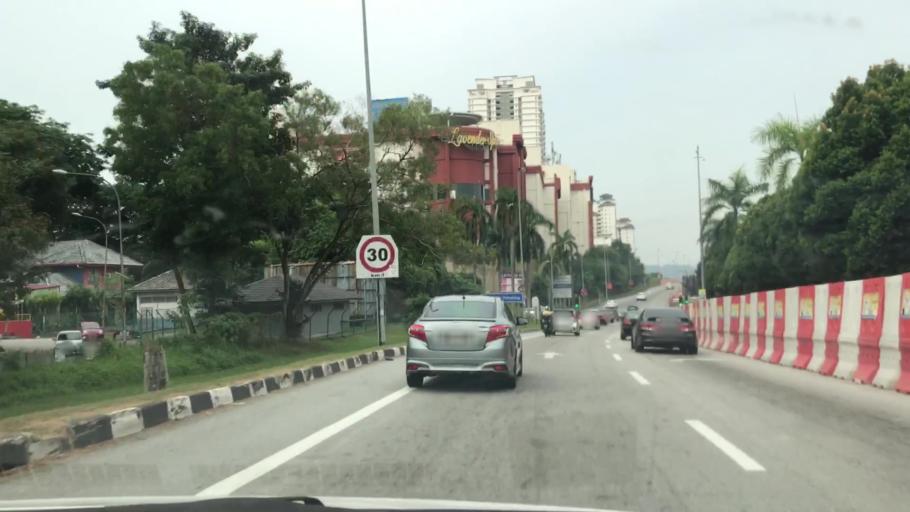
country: MY
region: Selangor
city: Kampong Baharu Balakong
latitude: 3.0627
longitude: 101.6926
